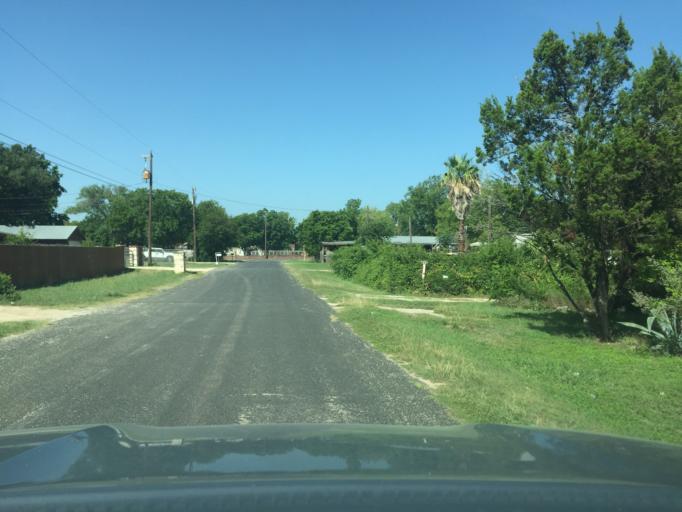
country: US
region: Texas
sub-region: Bexar County
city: Timberwood Park
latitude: 29.7048
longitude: -98.4781
